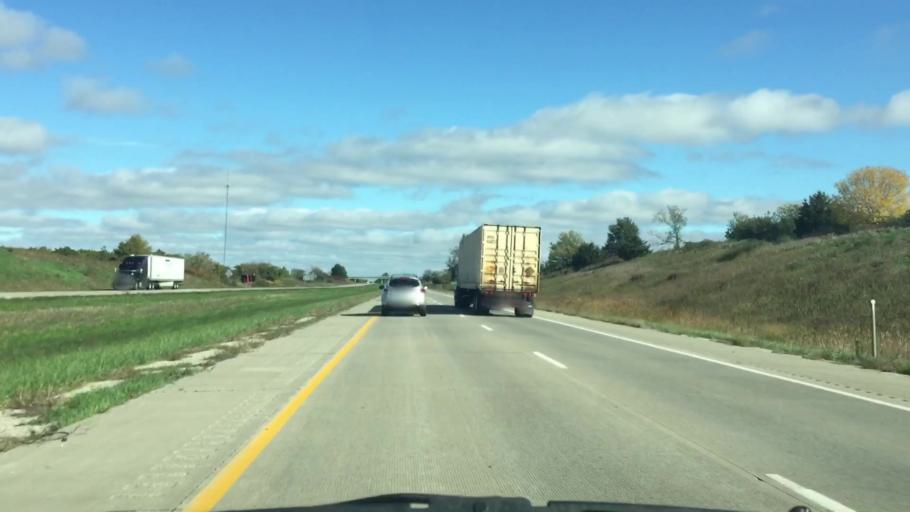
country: US
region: Iowa
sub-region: Decatur County
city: Leon
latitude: 40.7486
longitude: -93.8397
